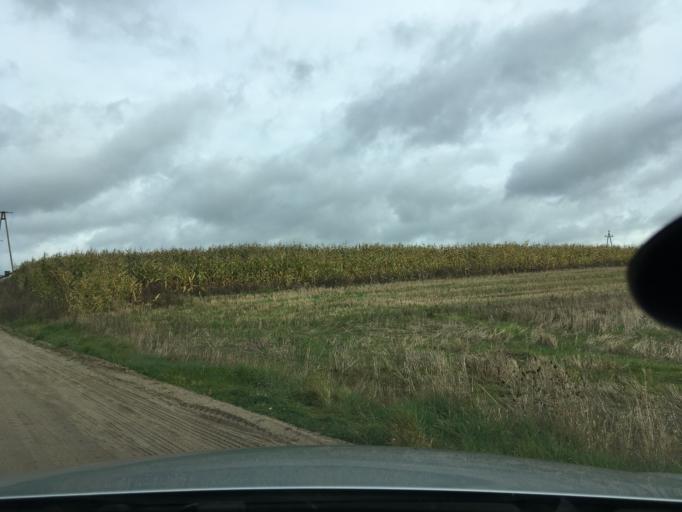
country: PL
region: Pomeranian Voivodeship
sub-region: Powiat koscierski
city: Koscierzyna
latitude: 54.1107
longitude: 18.0230
